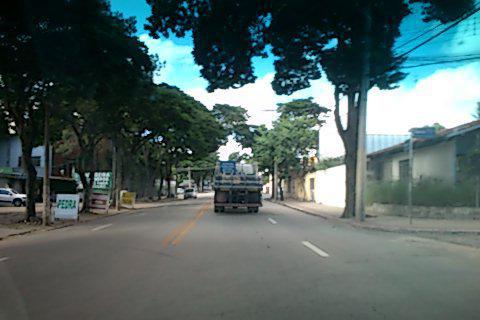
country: BR
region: Sao Paulo
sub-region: Sao Jose Dos Campos
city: Sao Jose dos Campos
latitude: -23.2107
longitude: -45.8852
